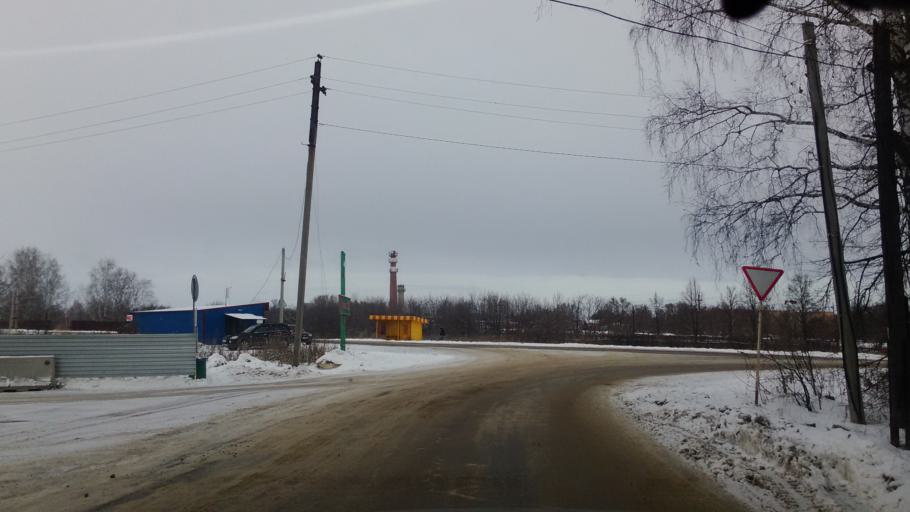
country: RU
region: Tula
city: Bogoroditsk
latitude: 53.7631
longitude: 38.1060
